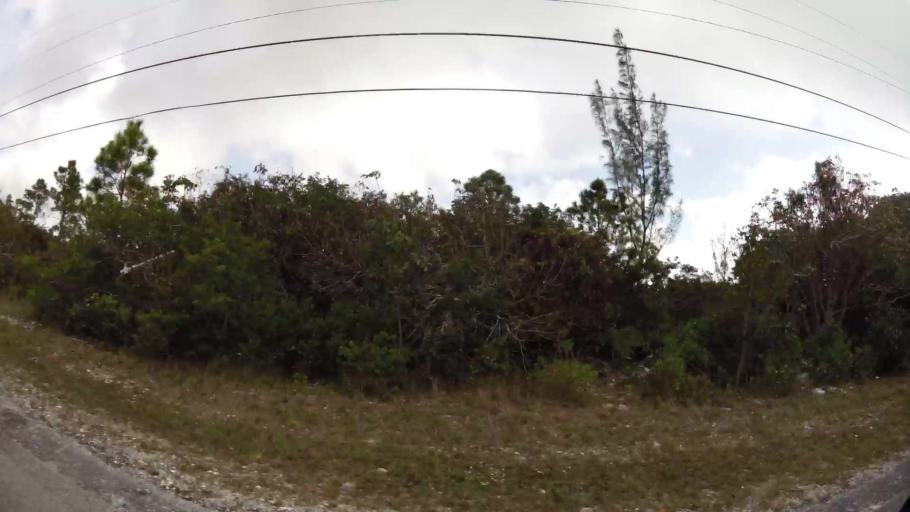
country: BS
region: Freeport
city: Lucaya
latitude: 26.5319
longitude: -78.6026
